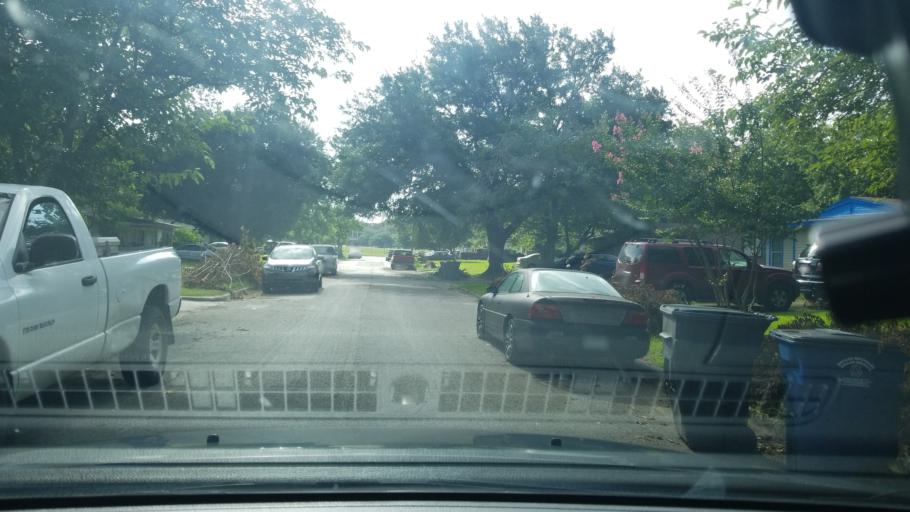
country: US
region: Texas
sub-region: Dallas County
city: Mesquite
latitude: 32.8160
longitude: -96.6643
